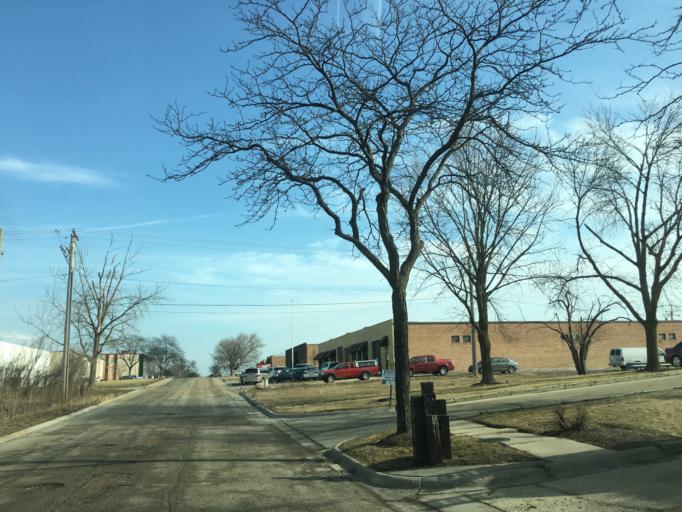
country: US
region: Illinois
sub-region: Cook County
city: Hoffman Estates
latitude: 42.0668
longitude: -88.0609
